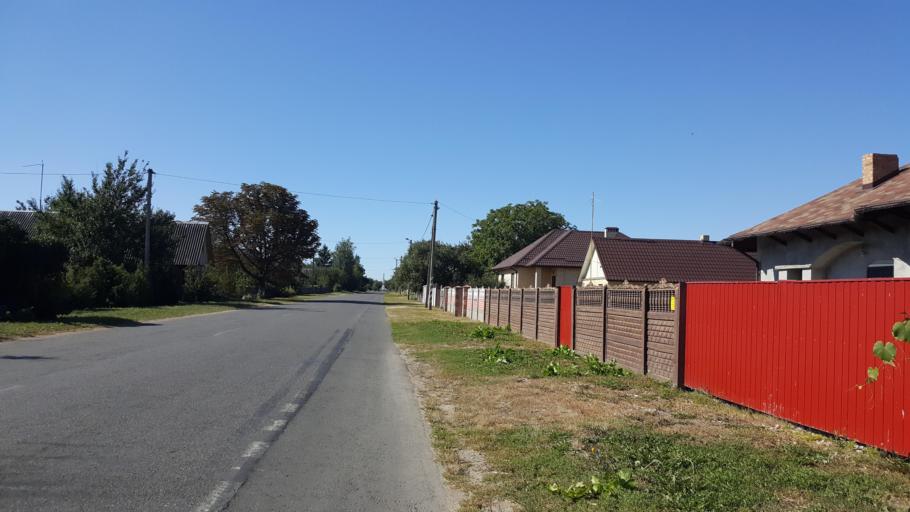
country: BY
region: Brest
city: Charnawchytsy
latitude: 52.2646
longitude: 23.5799
